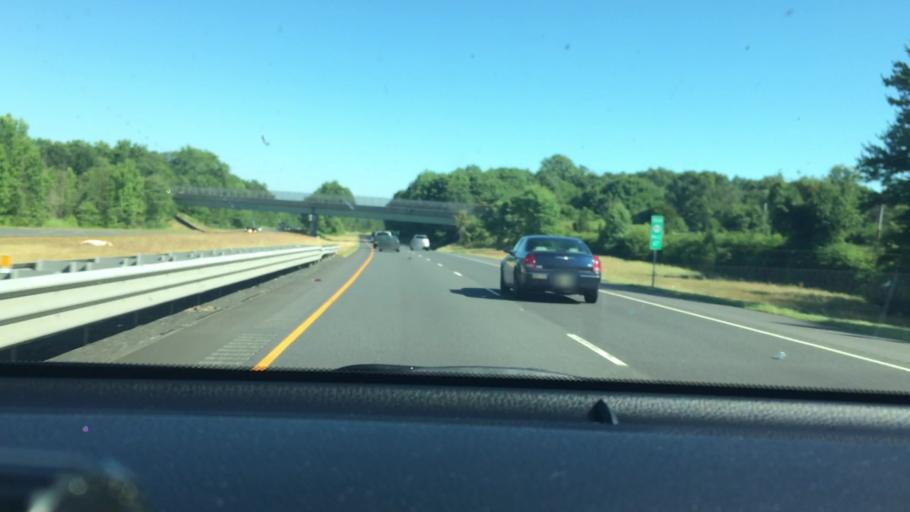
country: US
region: New Jersey
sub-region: Gloucester County
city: Glassboro
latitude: 39.6745
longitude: -75.1331
